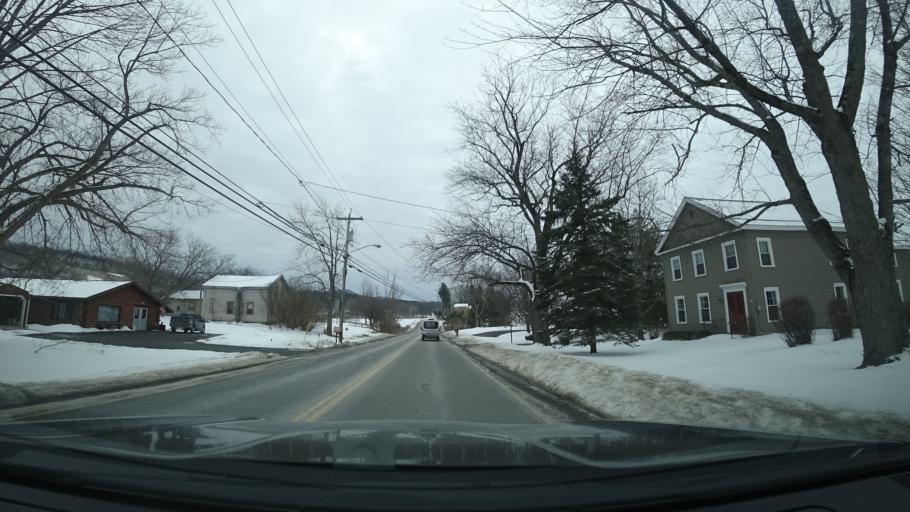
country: US
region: New York
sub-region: Washington County
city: Fort Edward
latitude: 43.2318
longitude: -73.4896
